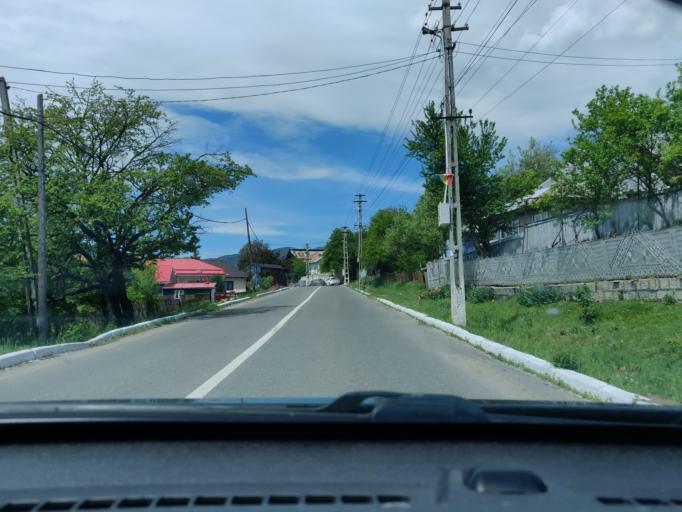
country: RO
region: Vrancea
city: Dragosloveni
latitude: 46.0001
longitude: 26.6641
